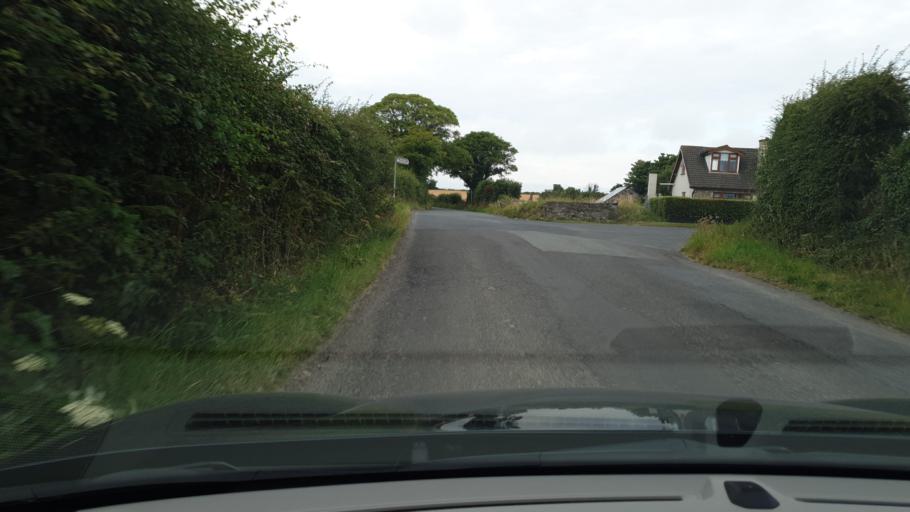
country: IE
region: Leinster
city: Balrothery
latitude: 53.5778
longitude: -6.1687
